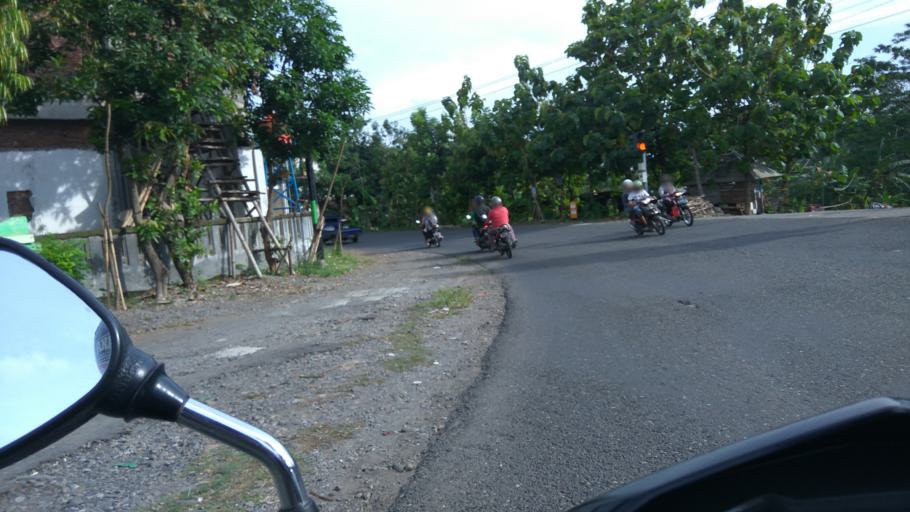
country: ID
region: Central Java
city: Mranggen
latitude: -7.0450
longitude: 110.4608
